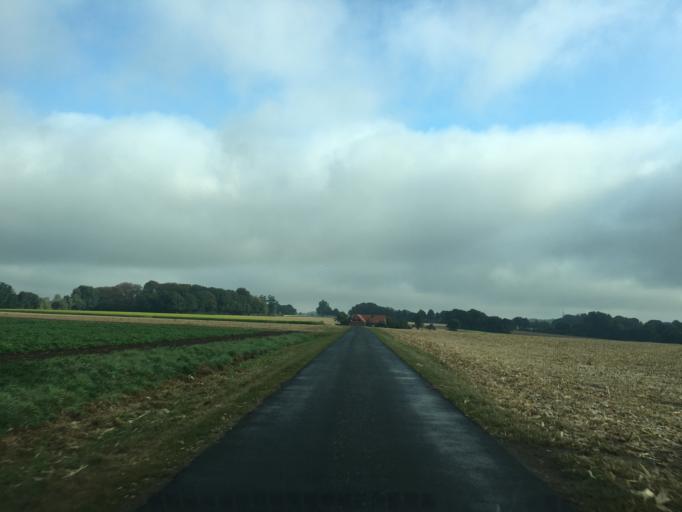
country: DE
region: North Rhine-Westphalia
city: Olfen
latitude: 51.7314
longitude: 7.3654
